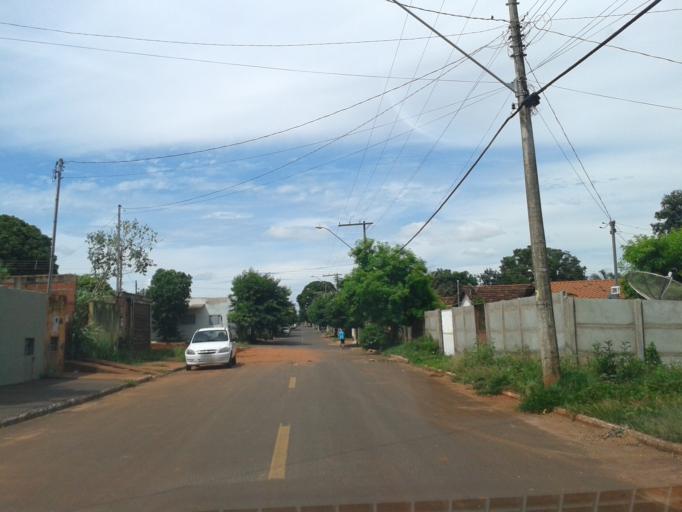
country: BR
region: Minas Gerais
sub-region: Santa Vitoria
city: Santa Vitoria
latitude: -18.8421
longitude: -50.1295
